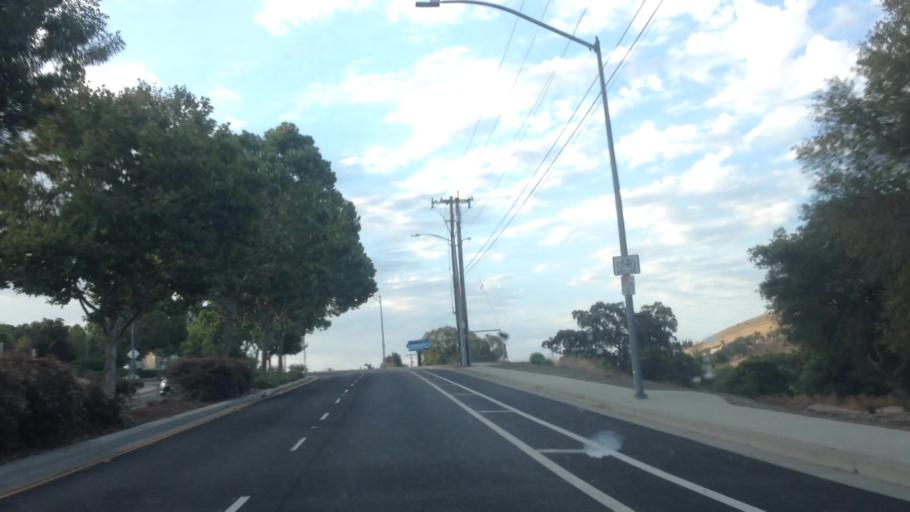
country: US
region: California
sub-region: Santa Clara County
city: Seven Trees
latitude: 37.2958
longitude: -121.7904
